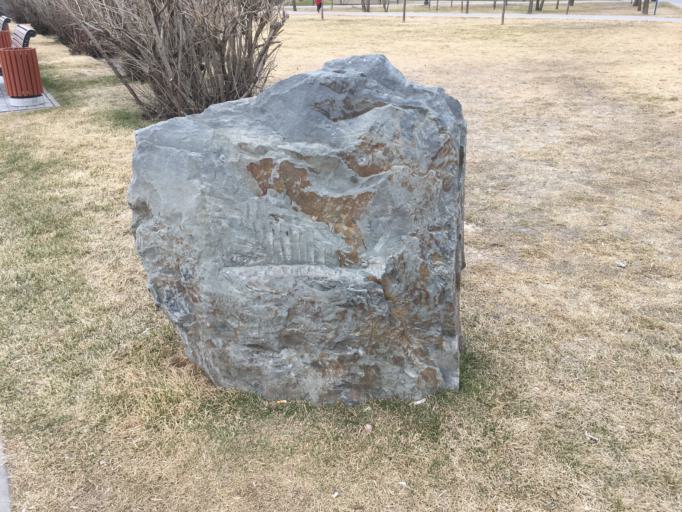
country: RU
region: Tomsk
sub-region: Tomskiy Rayon
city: Tomsk
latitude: 56.4745
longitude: 84.9512
